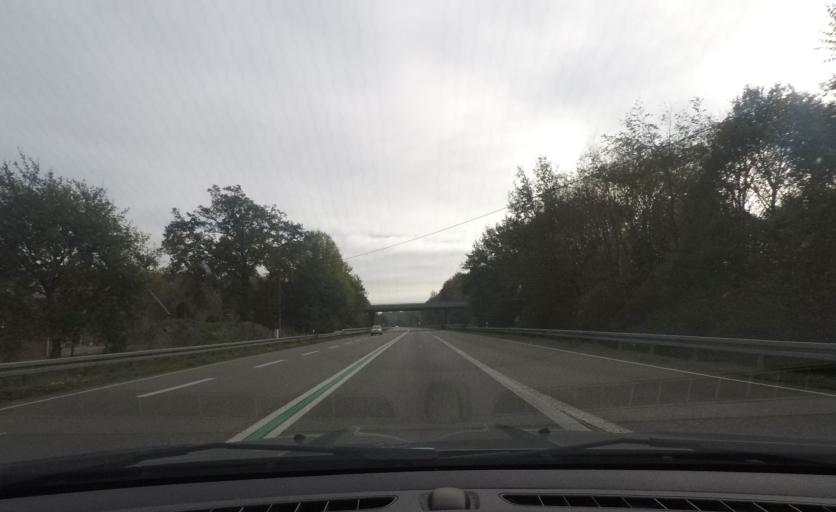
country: DE
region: North Rhine-Westphalia
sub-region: Regierungsbezirk Munster
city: Velen
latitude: 51.8568
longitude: 6.9745
